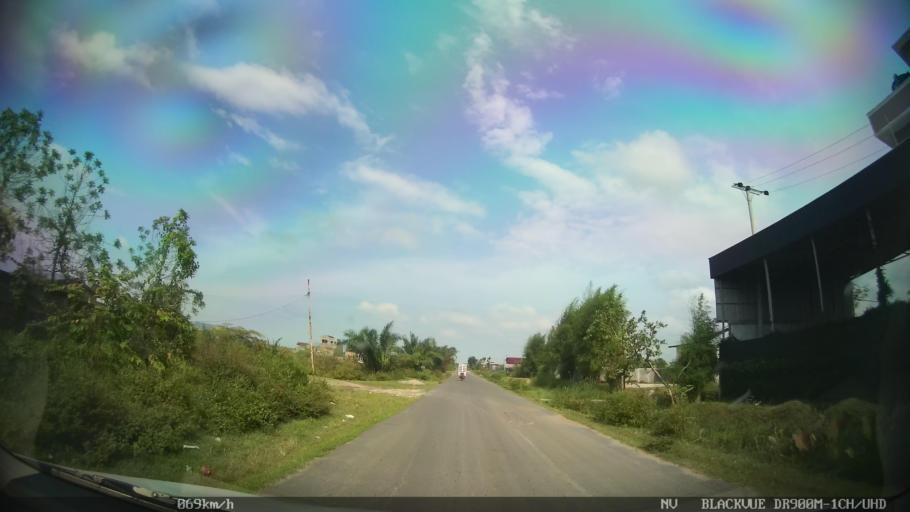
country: ID
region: North Sumatra
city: Medan
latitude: 3.5730
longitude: 98.7621
